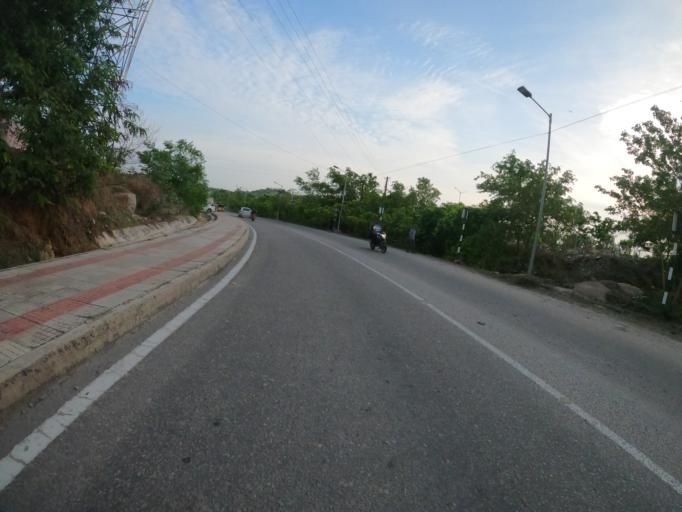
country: IN
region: Telangana
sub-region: Hyderabad
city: Hyderabad
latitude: 17.3854
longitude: 78.3517
